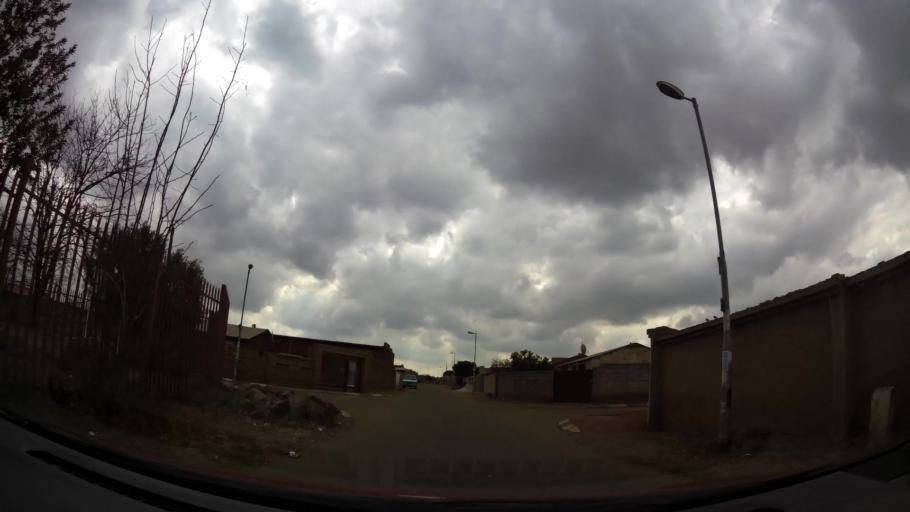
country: ZA
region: Gauteng
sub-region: City of Johannesburg Metropolitan Municipality
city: Soweto
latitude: -26.2574
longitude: 27.8416
